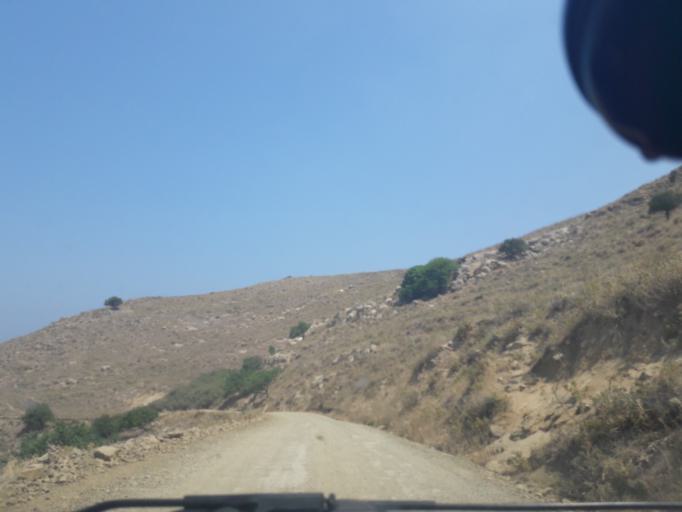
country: GR
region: North Aegean
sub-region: Nomos Lesvou
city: Myrina
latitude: 39.9725
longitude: 25.1524
